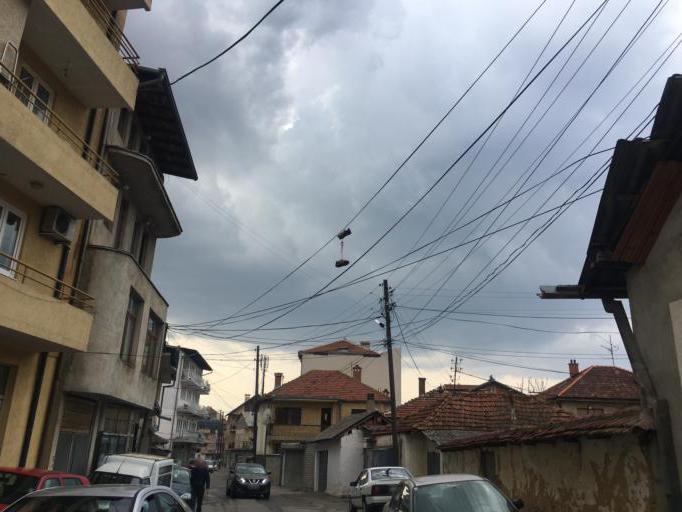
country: XK
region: Pristina
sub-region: Komuna e Prishtines
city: Pristina
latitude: 42.6655
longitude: 21.1726
